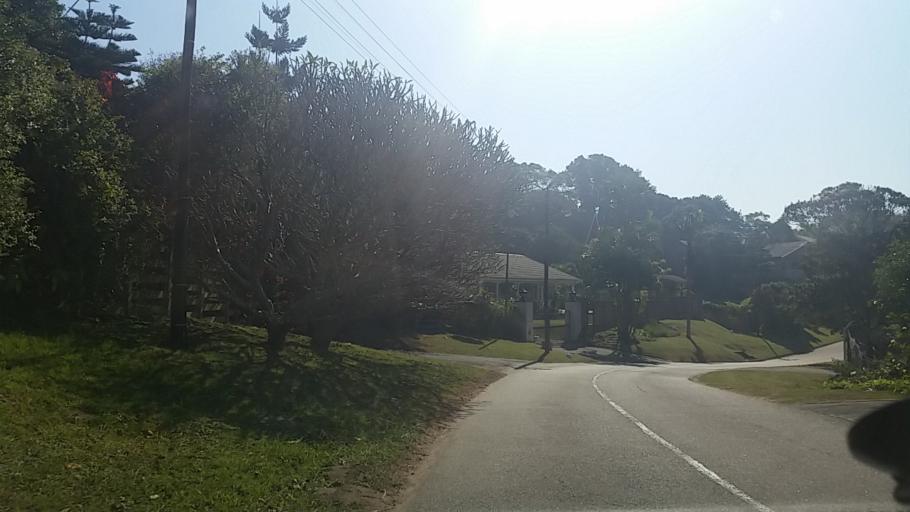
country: ZA
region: KwaZulu-Natal
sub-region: eThekwini Metropolitan Municipality
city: Berea
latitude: -29.8494
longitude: 30.9047
